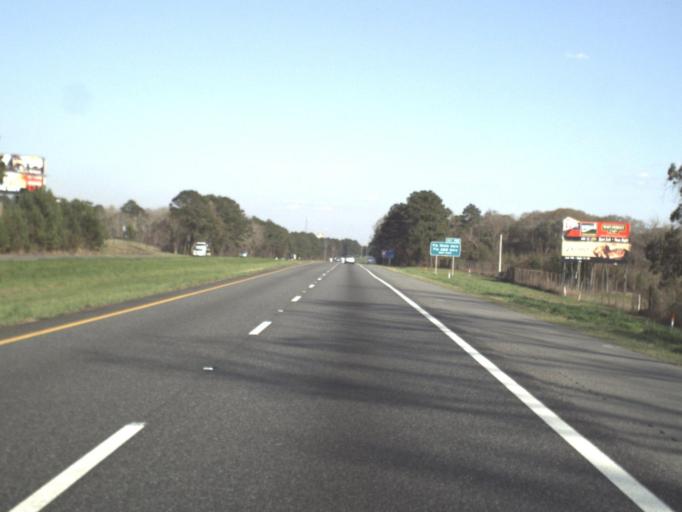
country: US
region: Florida
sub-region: Gadsden County
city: Midway
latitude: 30.4940
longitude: -84.4420
